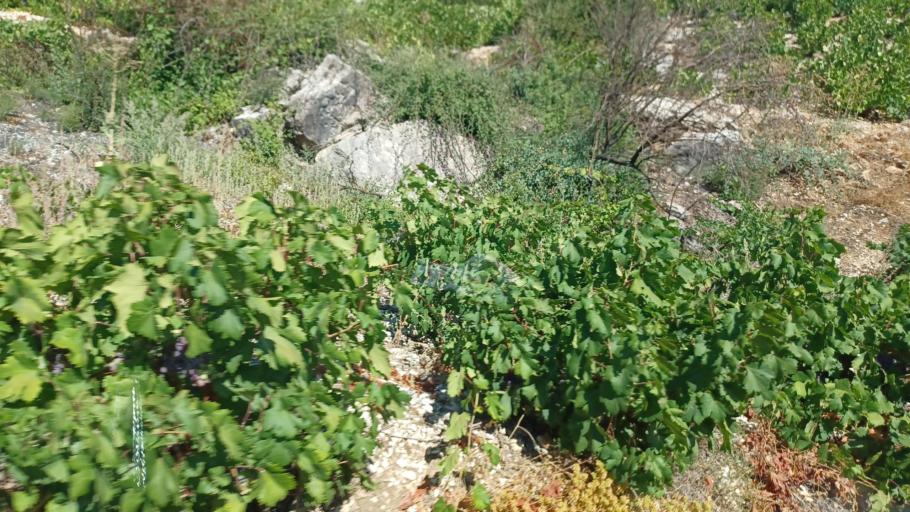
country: CY
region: Limassol
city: Pachna
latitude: 34.9004
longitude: 32.6436
